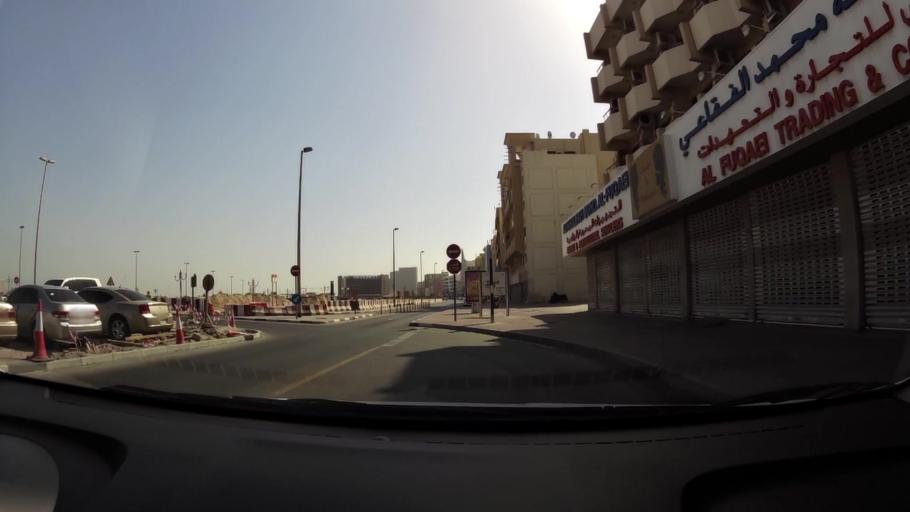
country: AE
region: Ash Shariqah
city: Sharjah
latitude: 25.2694
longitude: 55.2948
